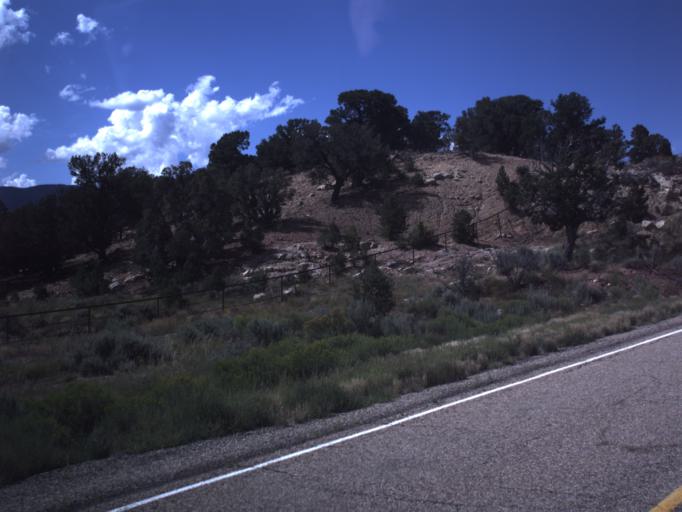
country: US
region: Utah
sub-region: Duchesne County
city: Duchesne
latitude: 40.2929
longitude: -110.6950
